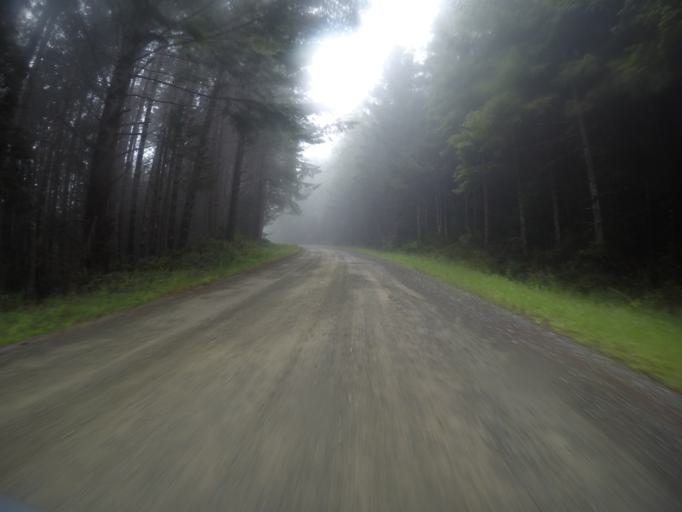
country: US
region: California
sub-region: Humboldt County
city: Westhaven-Moonstone
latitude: 41.2354
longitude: -123.9930
